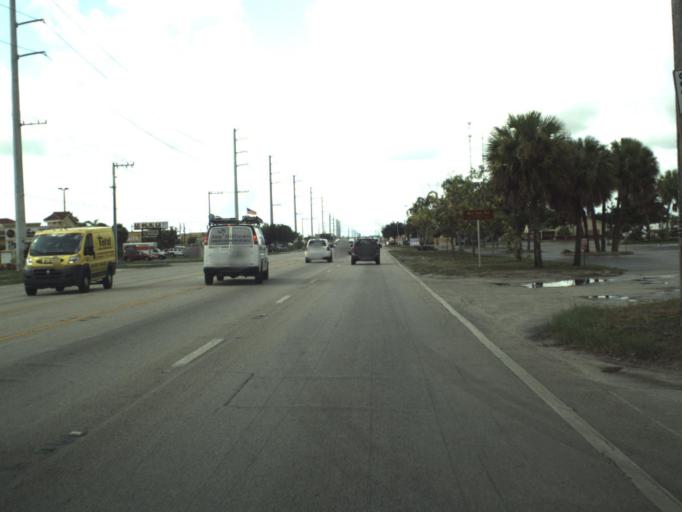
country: US
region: Florida
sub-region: Broward County
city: West Park
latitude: 25.9936
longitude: -80.2071
